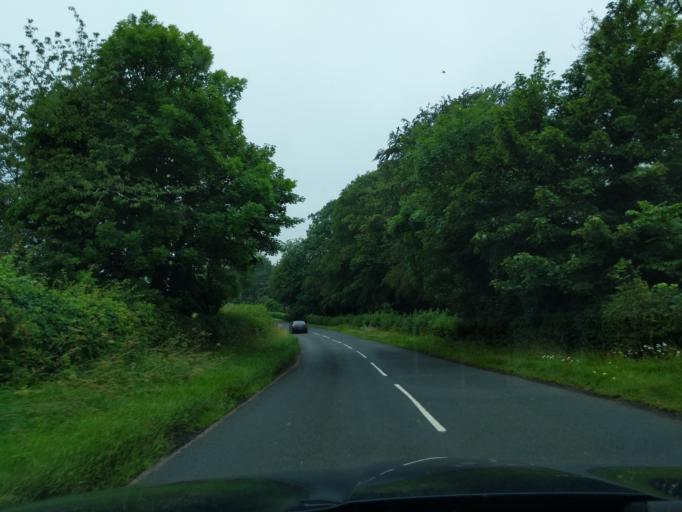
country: GB
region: England
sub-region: Northumberland
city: Lowick
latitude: 55.6602
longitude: -1.9291
